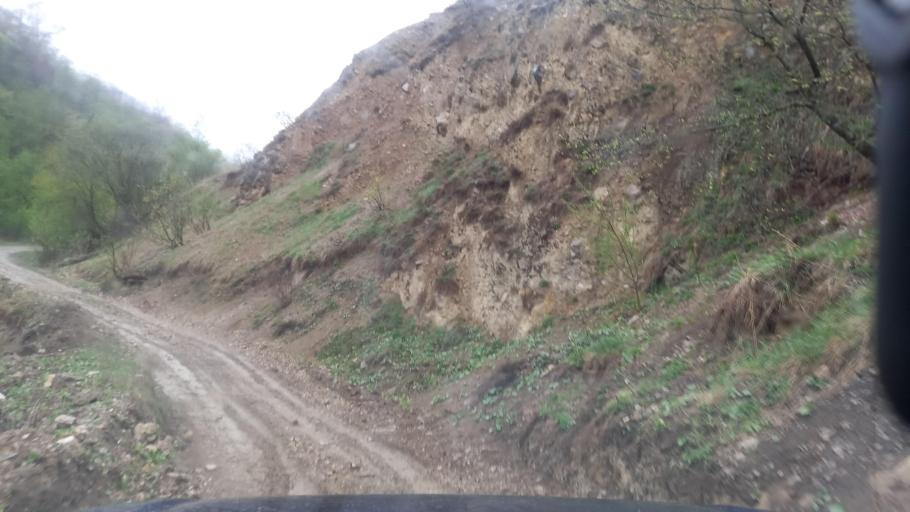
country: RU
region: Kabardino-Balkariya
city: Bylym
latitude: 43.6003
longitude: 42.9341
